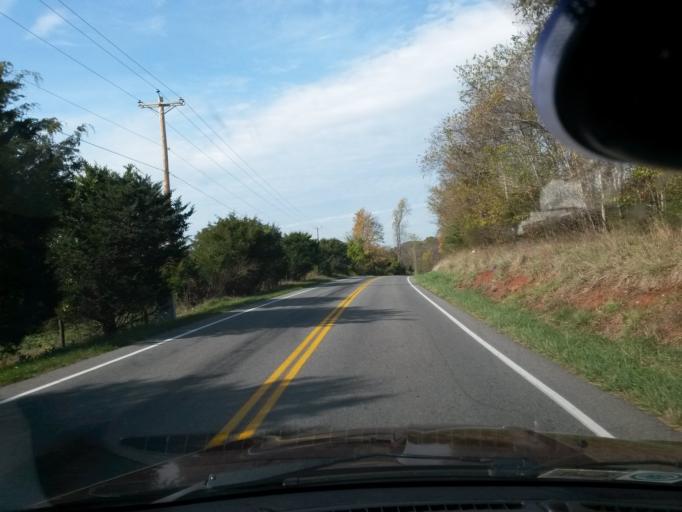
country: US
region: Virginia
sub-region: Franklin County
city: North Shore
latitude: 37.1277
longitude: -79.7550
